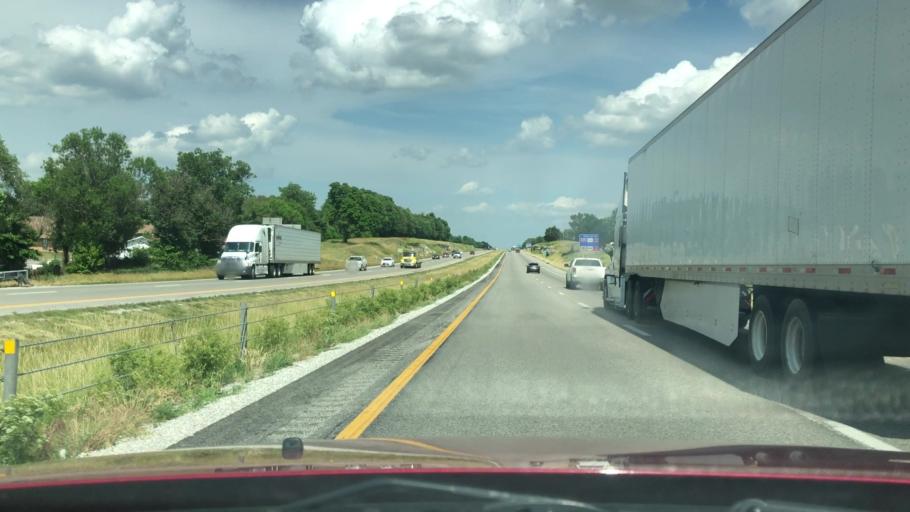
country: US
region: Missouri
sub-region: Greene County
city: Springfield
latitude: 37.2502
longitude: -93.2906
